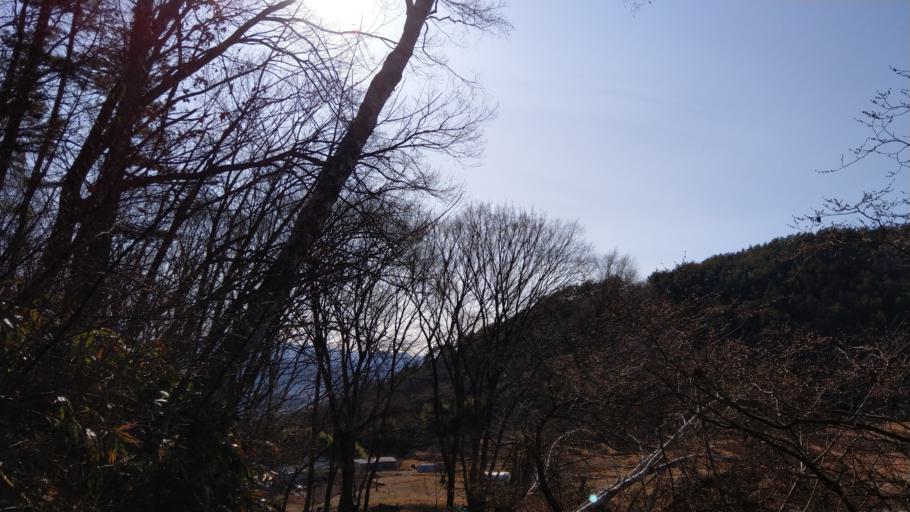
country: JP
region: Nagano
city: Ueda
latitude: 36.3797
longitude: 138.3563
